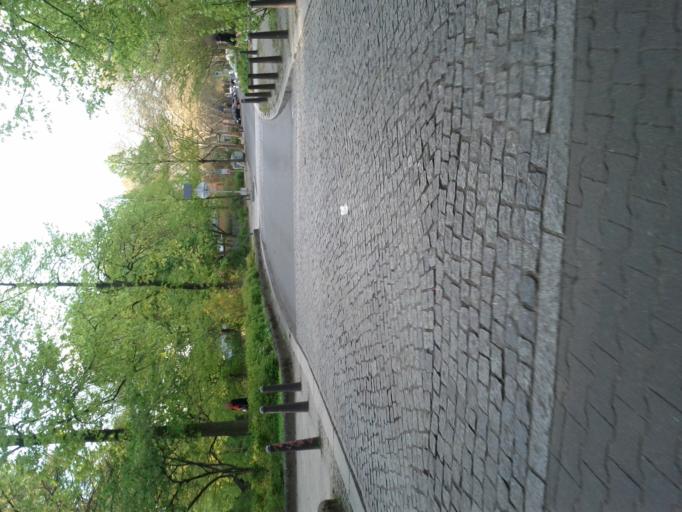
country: DE
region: Berlin
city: Friedenau
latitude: 52.4815
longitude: 13.3333
